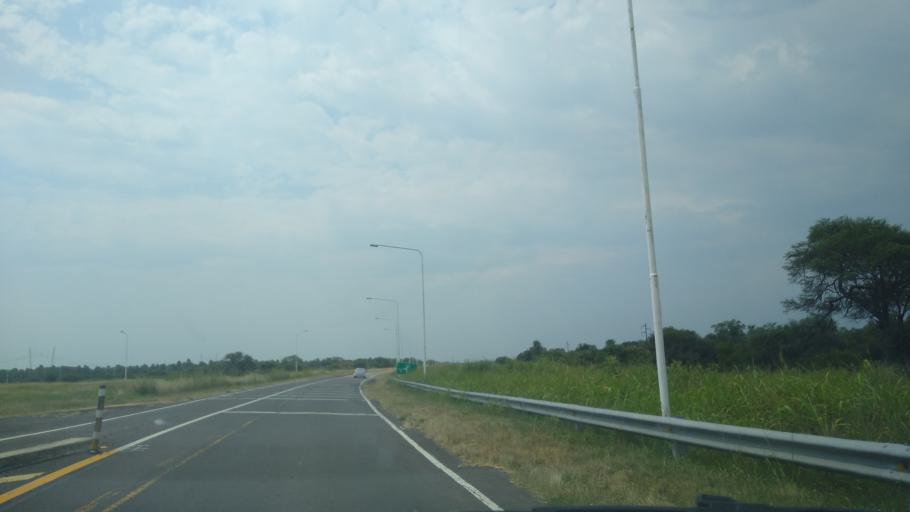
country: AR
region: Chaco
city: Margarita Belen
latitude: -27.0895
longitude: -58.9583
